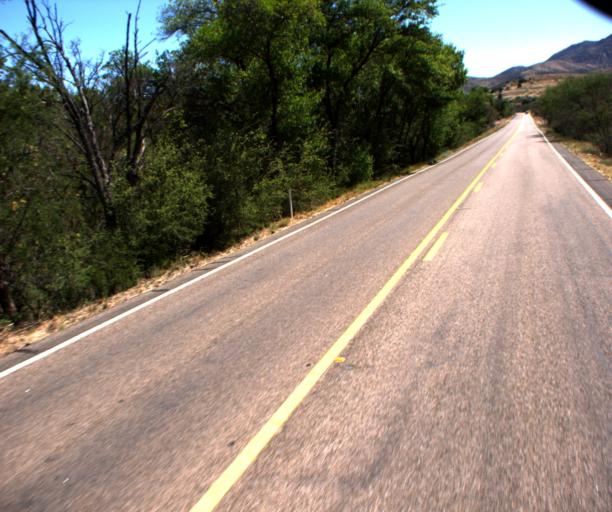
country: US
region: Arizona
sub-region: Santa Cruz County
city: Rio Rico
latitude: 31.5153
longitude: -110.7924
